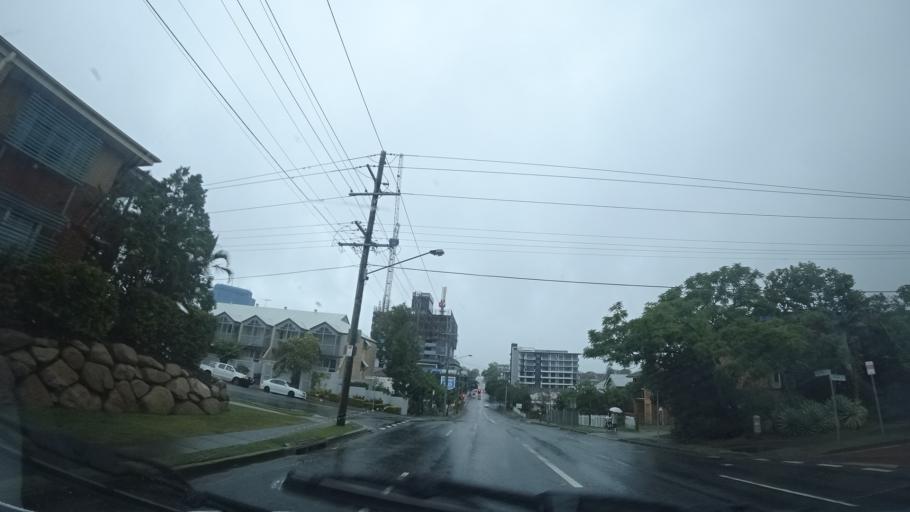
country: AU
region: Queensland
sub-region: Brisbane
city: Toowong
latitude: -27.4827
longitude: 152.9910
